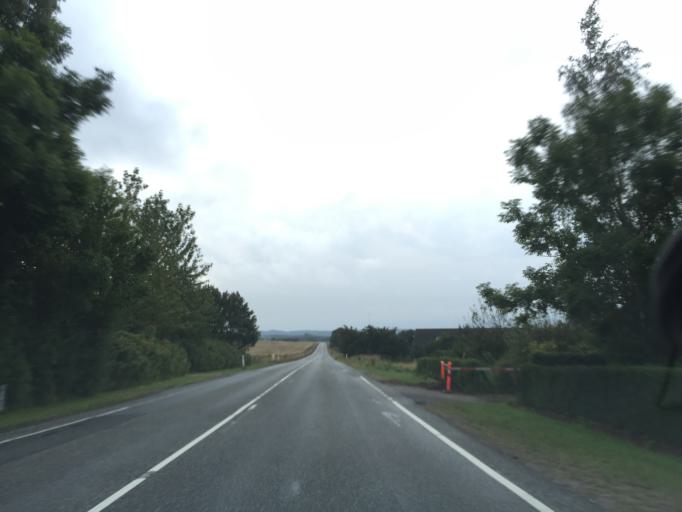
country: DK
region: Central Jutland
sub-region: Skanderborg Kommune
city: Ry
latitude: 56.1355
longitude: 9.8272
